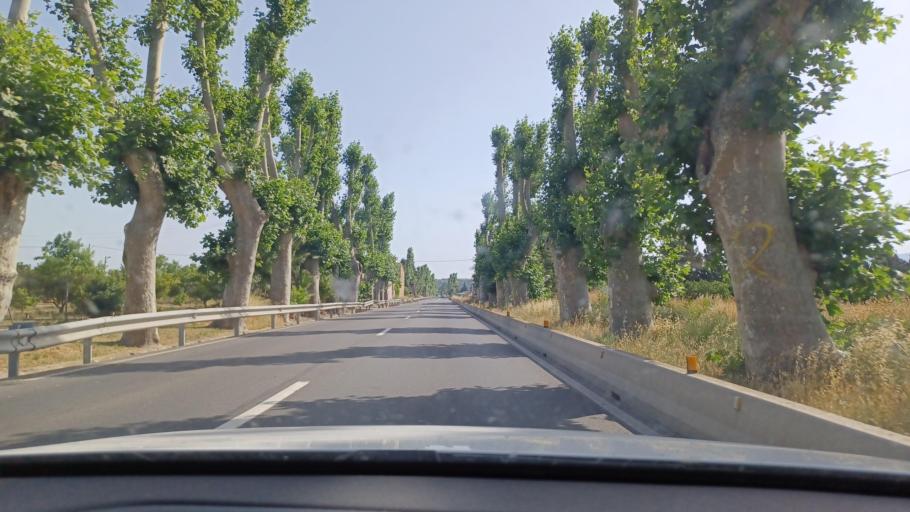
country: ES
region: Catalonia
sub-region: Provincia de Tarragona
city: Tortosa
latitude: 40.8014
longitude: 0.5020
